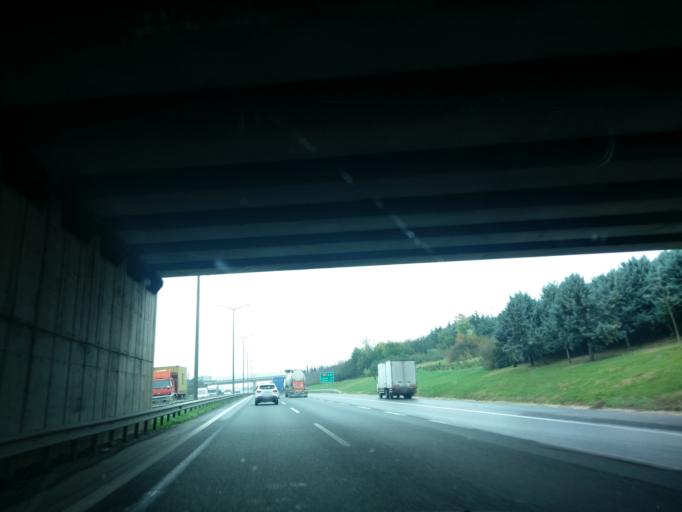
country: TR
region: Istanbul
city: Silivri
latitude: 41.1115
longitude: 28.2646
